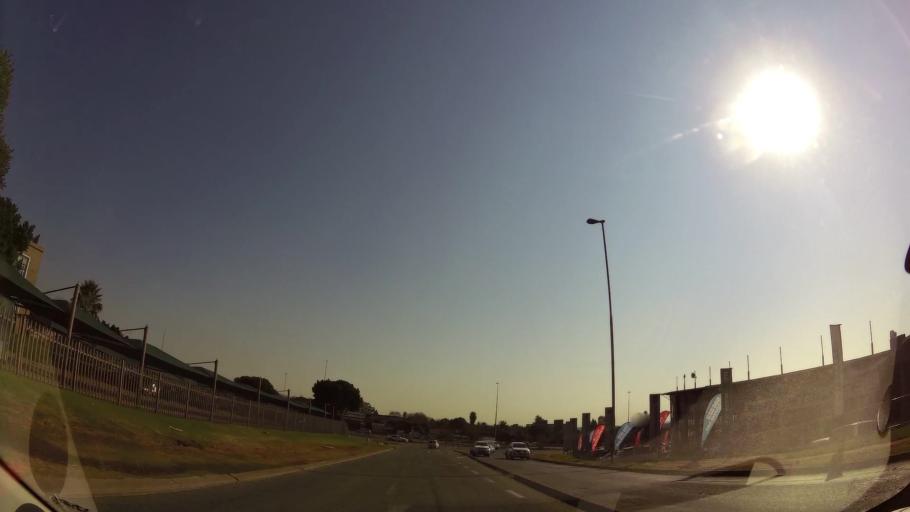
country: ZA
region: Gauteng
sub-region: City of Johannesburg Metropolitan Municipality
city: Modderfontein
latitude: -26.1559
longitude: 28.1663
